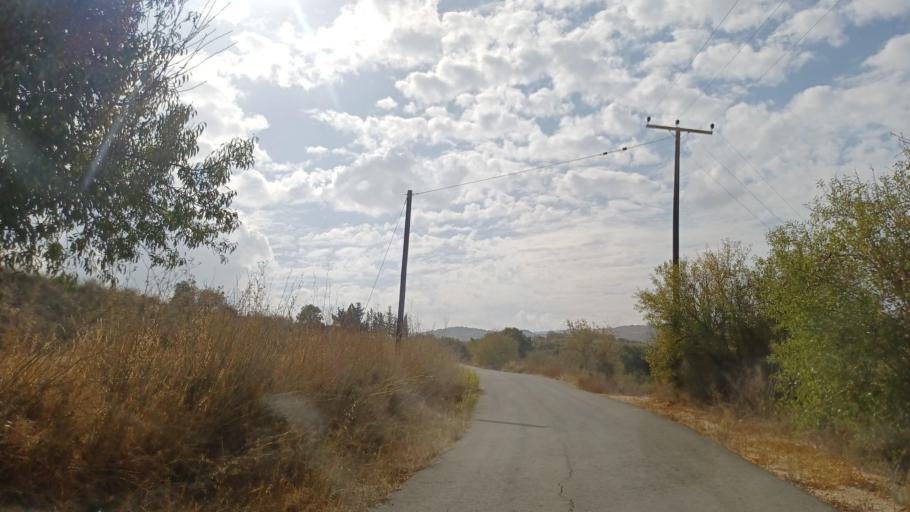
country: CY
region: Pafos
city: Polis
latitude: 35.0218
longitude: 32.4177
